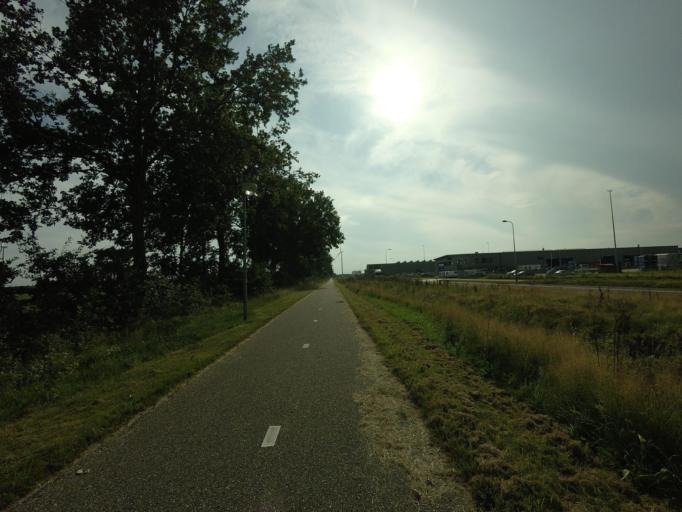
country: NL
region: Drenthe
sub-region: Gemeente Coevorden
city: Coevorden
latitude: 52.6511
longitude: 6.7257
